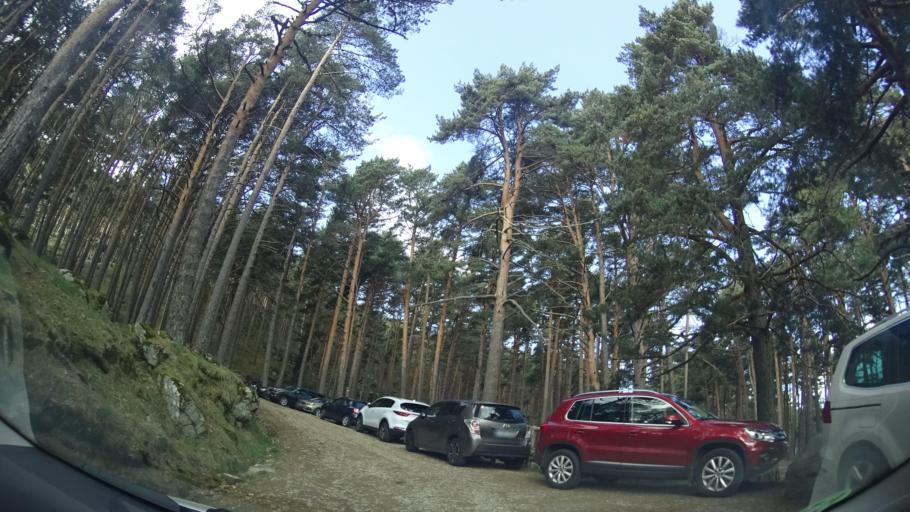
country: ES
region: Madrid
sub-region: Provincia de Madrid
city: Canencia
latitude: 40.8694
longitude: -3.7648
